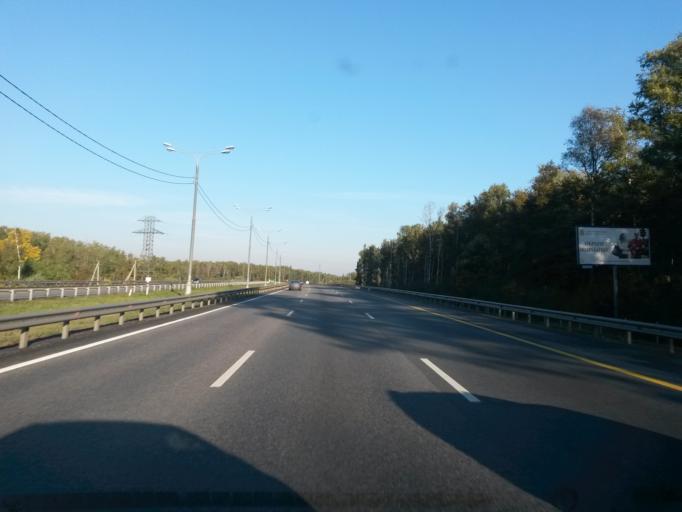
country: RU
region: Moskovskaya
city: Vostryakovo
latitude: 55.3613
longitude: 37.7935
